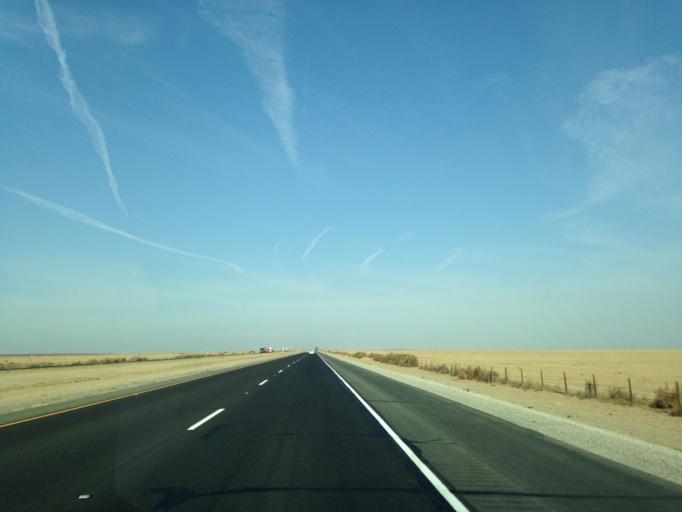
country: US
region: California
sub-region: Kern County
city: Lost Hills
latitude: 35.6388
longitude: -119.6698
